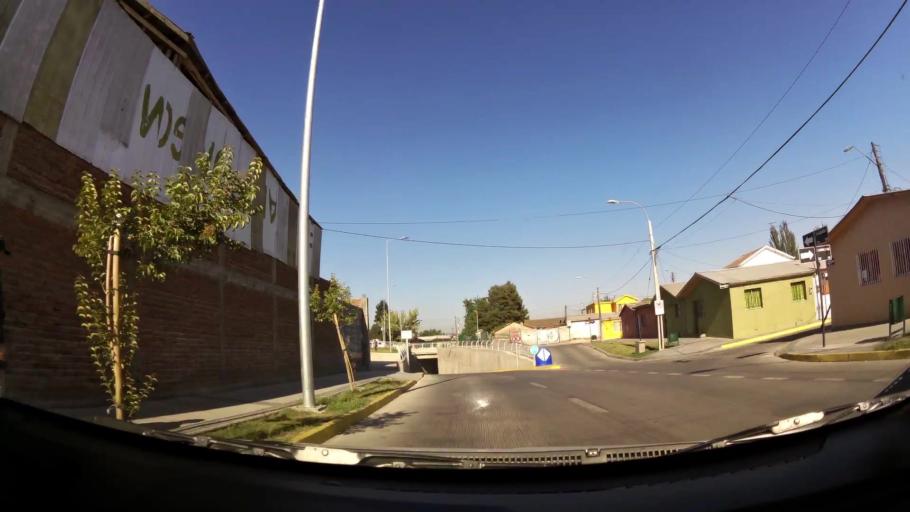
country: CL
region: Maule
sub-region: Provincia de Curico
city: Curico
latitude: -34.9875
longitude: -71.2447
